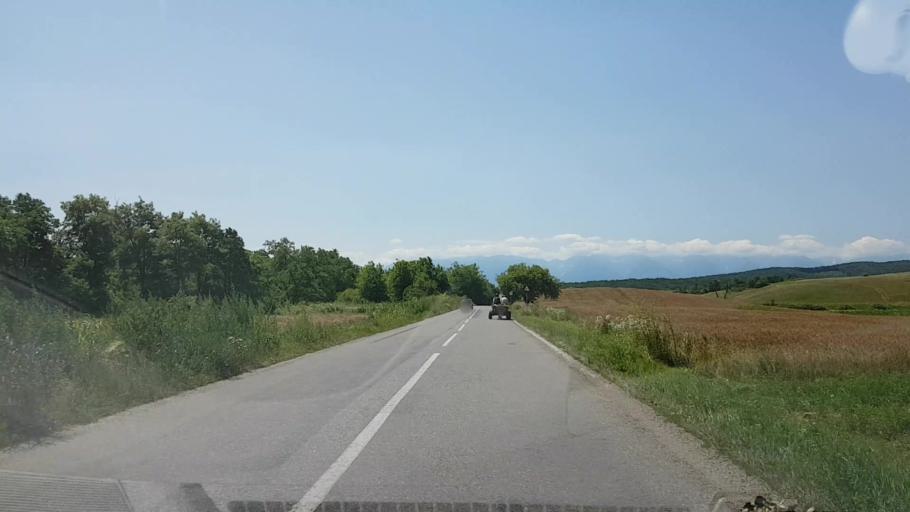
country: RO
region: Brasov
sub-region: Comuna Cincu
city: Cincu
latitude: 45.8995
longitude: 24.8120
